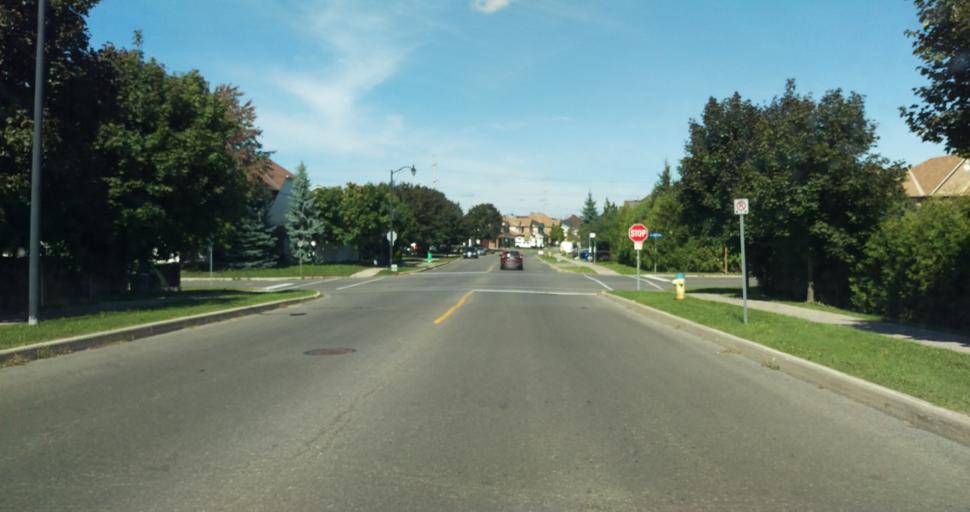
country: CA
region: Ontario
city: Clarence-Rockland
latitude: 45.4596
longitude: -75.4759
